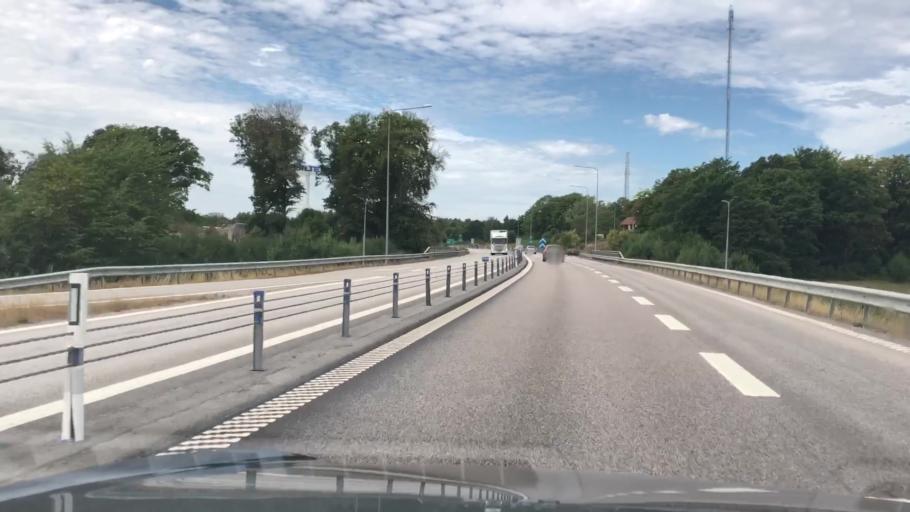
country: SE
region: Blekinge
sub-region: Karlskrona Kommun
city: Rodeby
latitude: 56.2060
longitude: 15.6428
